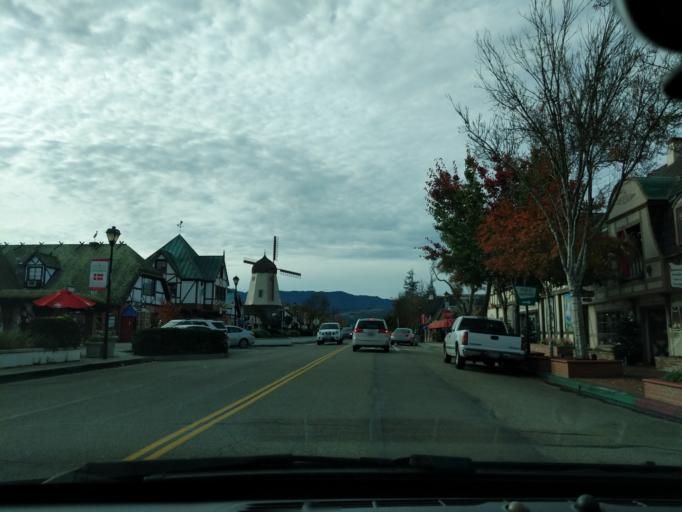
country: US
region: California
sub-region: Santa Barbara County
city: Solvang
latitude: 34.5951
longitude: -120.1385
